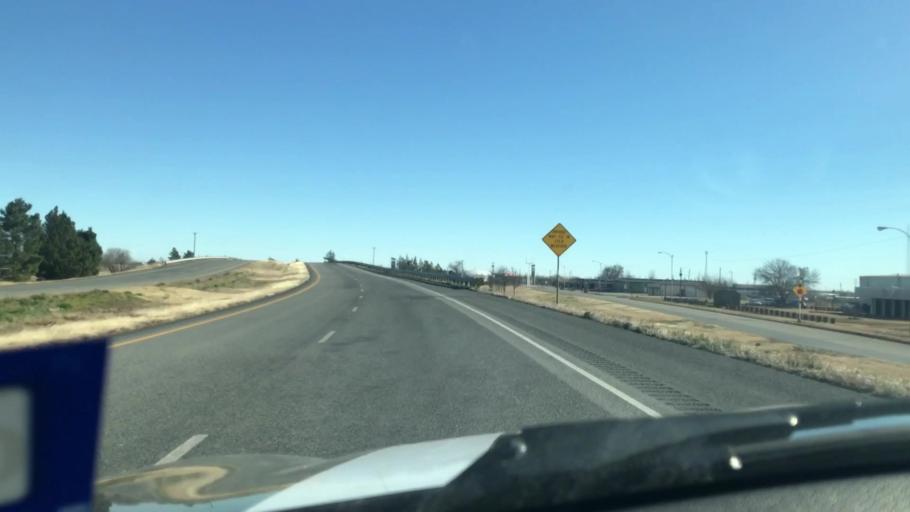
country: US
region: Texas
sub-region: Scurry County
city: Snyder
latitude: 32.7411
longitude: -100.9209
